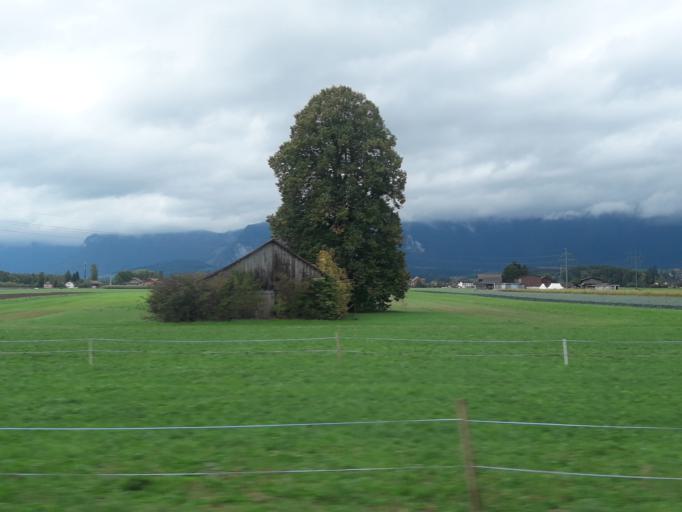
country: CH
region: Bern
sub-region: Thun District
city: Uetendorf
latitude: 46.7734
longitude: 7.5905
